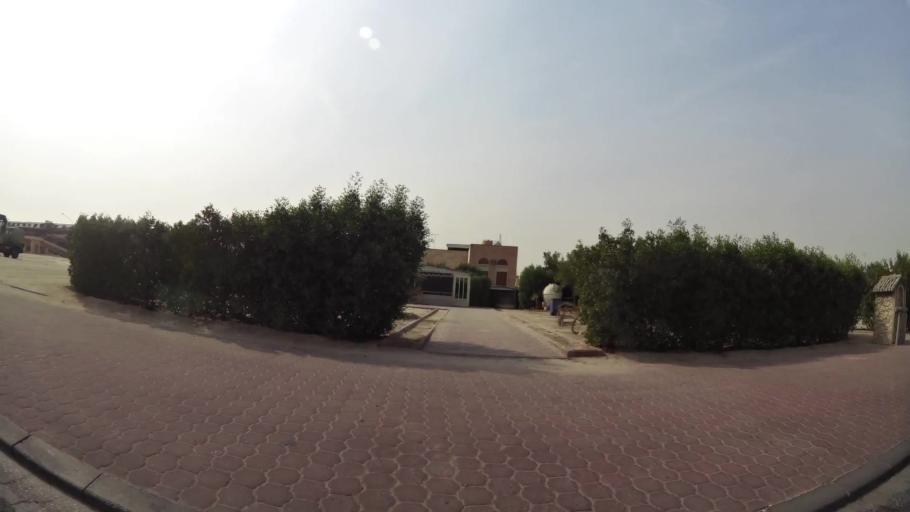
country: KW
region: Al Asimah
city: Ar Rabiyah
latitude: 29.2896
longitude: 47.9395
